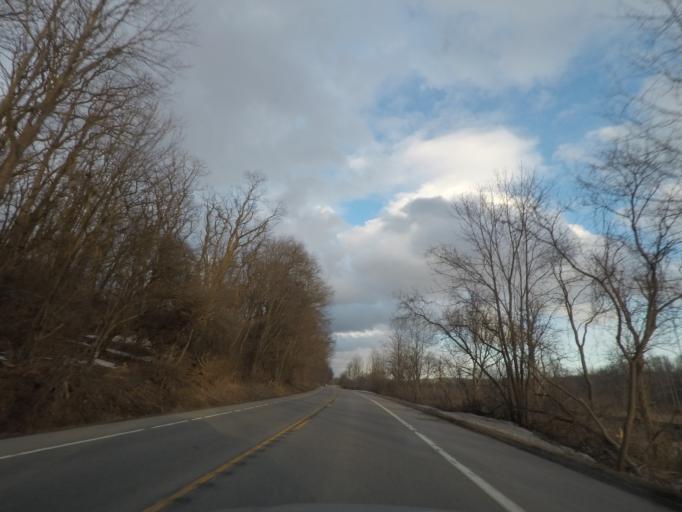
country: US
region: New York
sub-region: Montgomery County
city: Saint Johnsville
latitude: 43.0080
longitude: -74.7579
